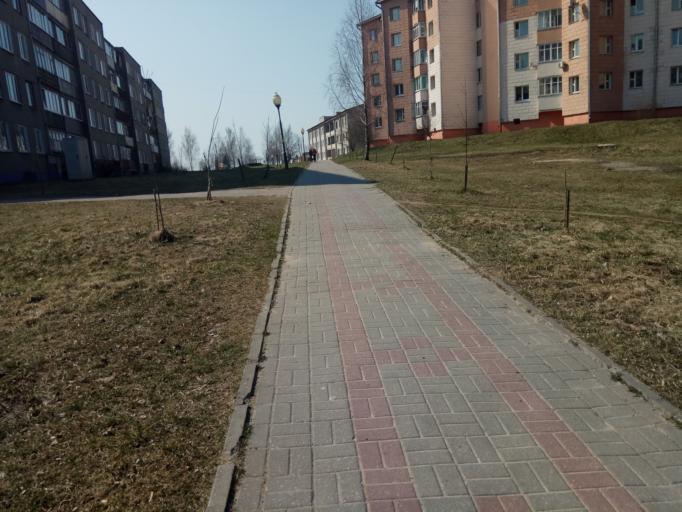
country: BY
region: Minsk
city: Valozhyn
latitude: 54.0873
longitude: 26.5207
